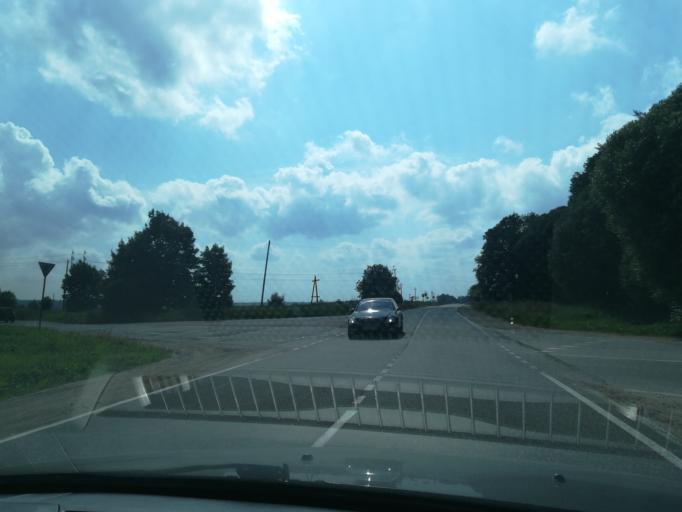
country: RU
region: Leningrad
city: Kopor'ye
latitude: 59.7036
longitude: 29.0546
